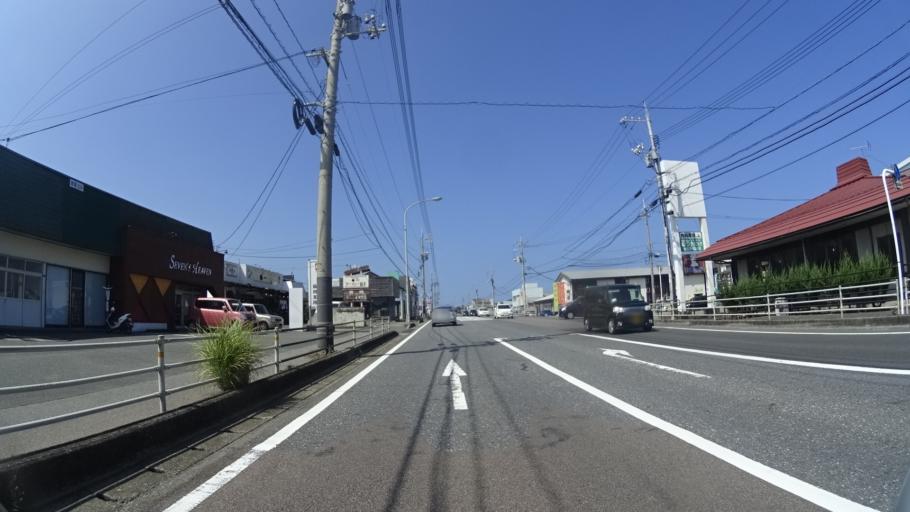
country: JP
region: Shimane
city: Masuda
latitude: 34.6899
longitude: 131.8139
